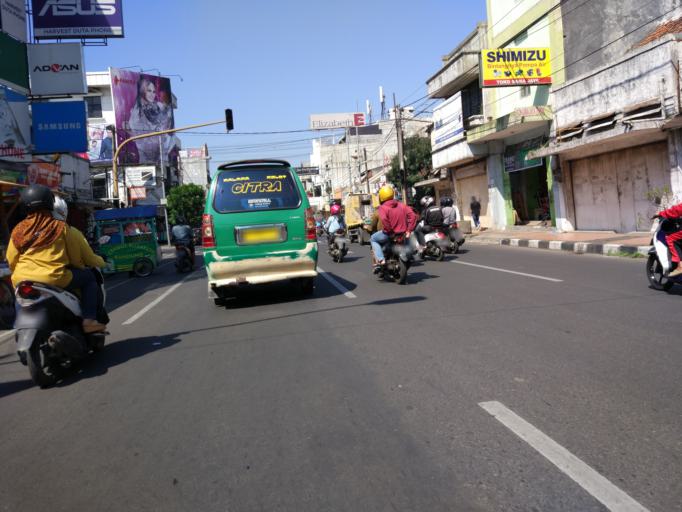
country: ID
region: West Java
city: Bandung
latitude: -6.9310
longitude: 107.6034
